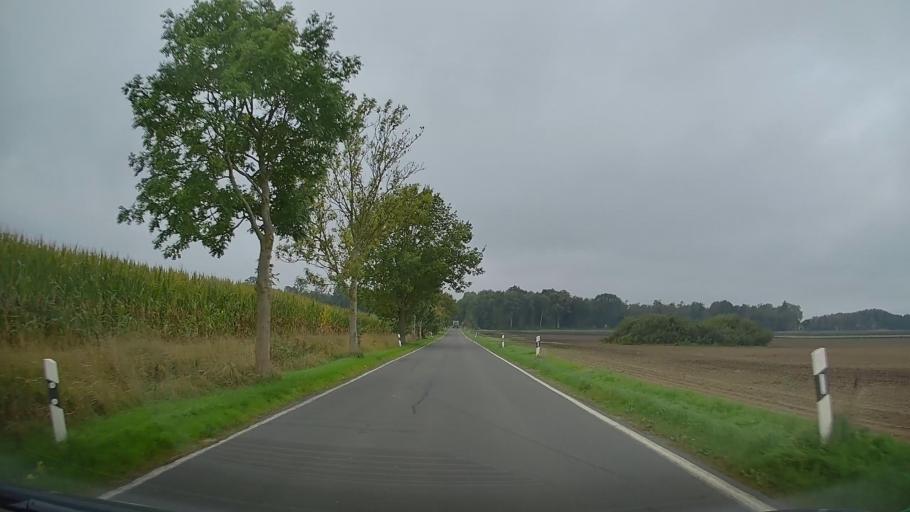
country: DE
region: Mecklenburg-Vorpommern
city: Dummerstorf
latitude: 53.9782
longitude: 12.2667
